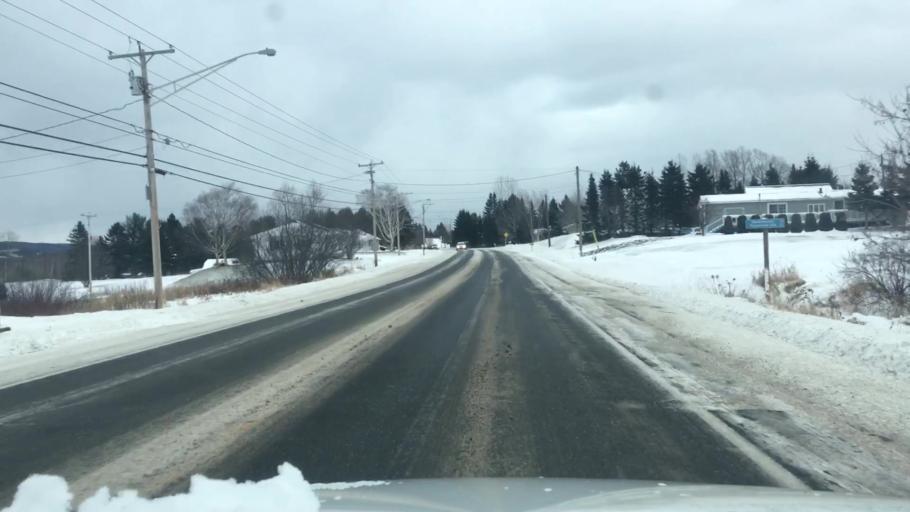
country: US
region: Maine
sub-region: Aroostook County
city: Madawaska
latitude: 47.3469
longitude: -68.2664
